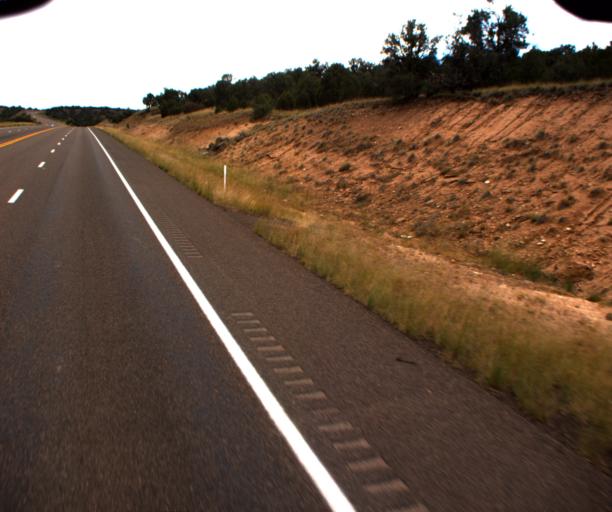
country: US
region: Arizona
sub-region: Navajo County
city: White Mountain Lake
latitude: 34.3840
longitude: -110.0601
